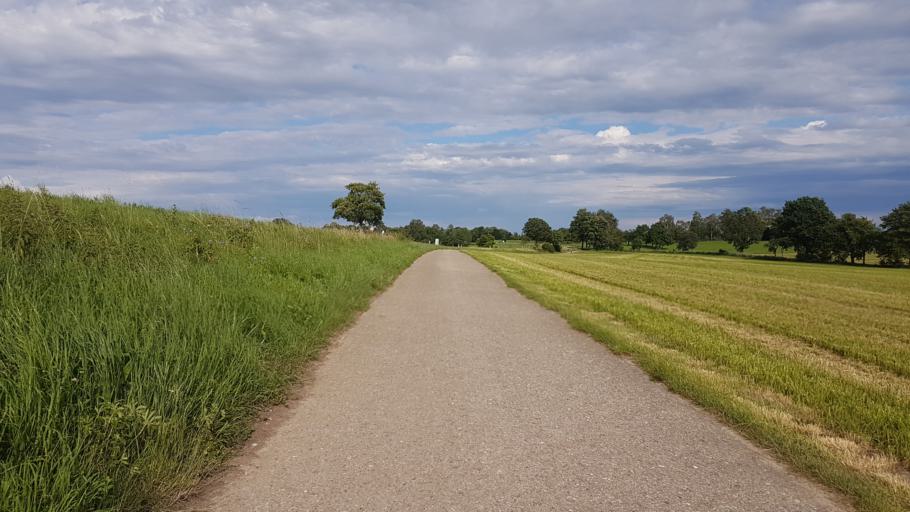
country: DE
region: Baden-Wuerttemberg
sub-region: Tuebingen Region
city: Rottenacker
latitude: 48.2308
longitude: 9.6686
